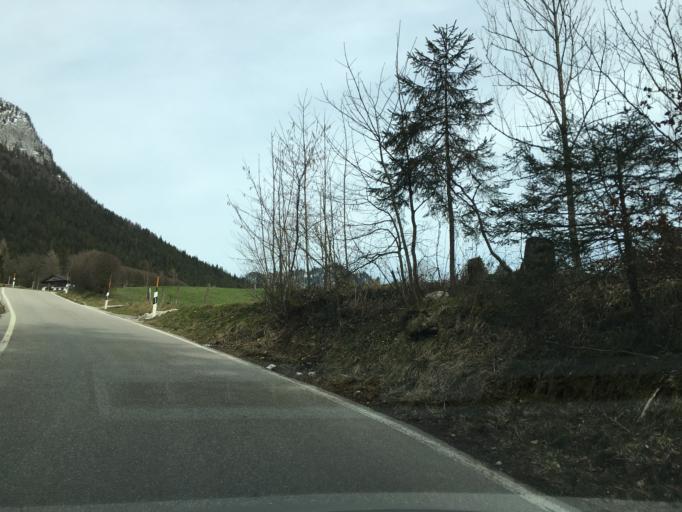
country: DE
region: Bavaria
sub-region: Upper Bavaria
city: Ramsau
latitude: 47.6109
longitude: 12.8608
